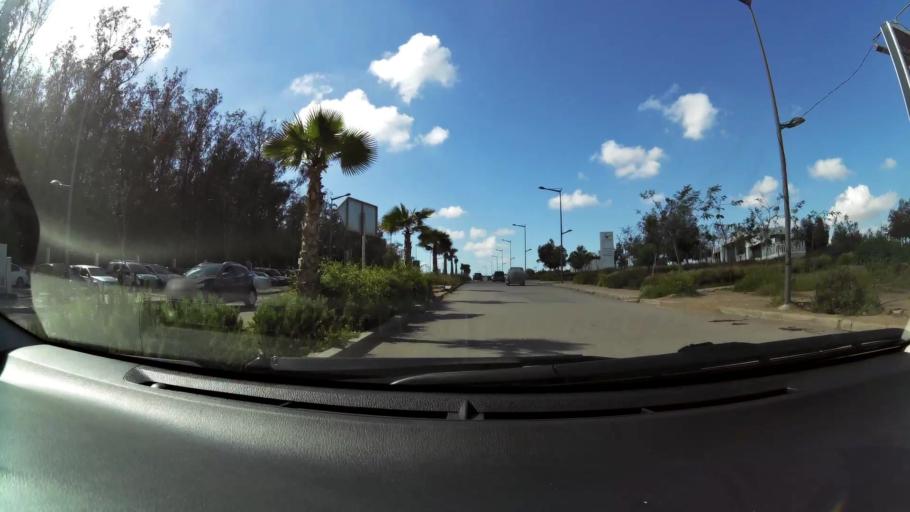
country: MA
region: Grand Casablanca
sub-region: Nouaceur
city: Bouskoura
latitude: 33.4790
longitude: -7.6223
